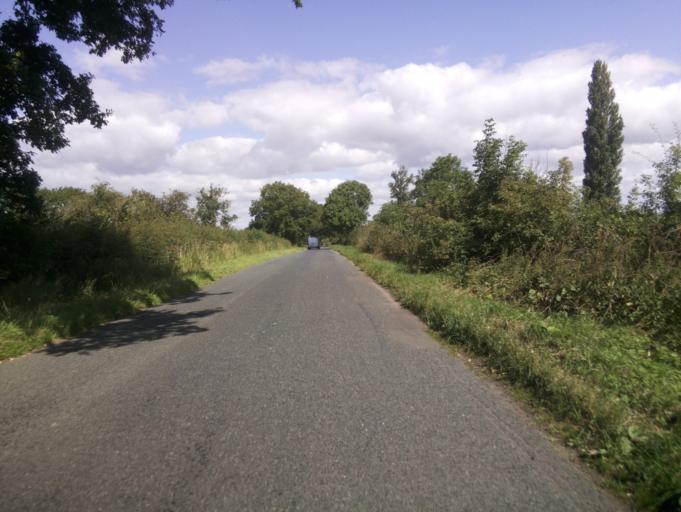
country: GB
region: England
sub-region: Milton Keynes
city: Calverton
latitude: 51.9931
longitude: -0.8598
